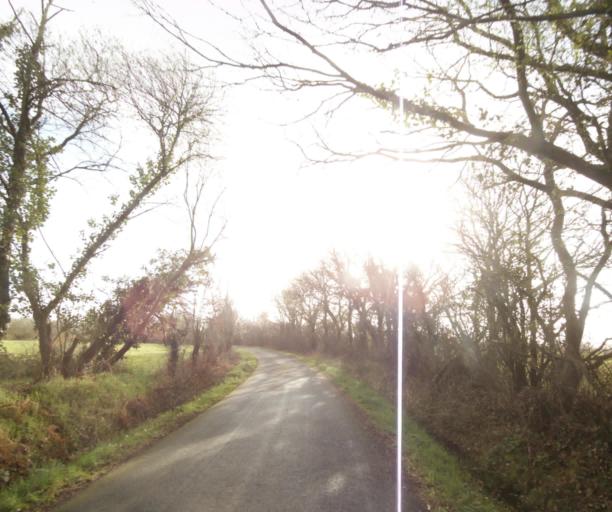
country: FR
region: Pays de la Loire
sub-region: Departement de la Loire-Atlantique
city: Malville
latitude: 47.3961
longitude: -1.8877
